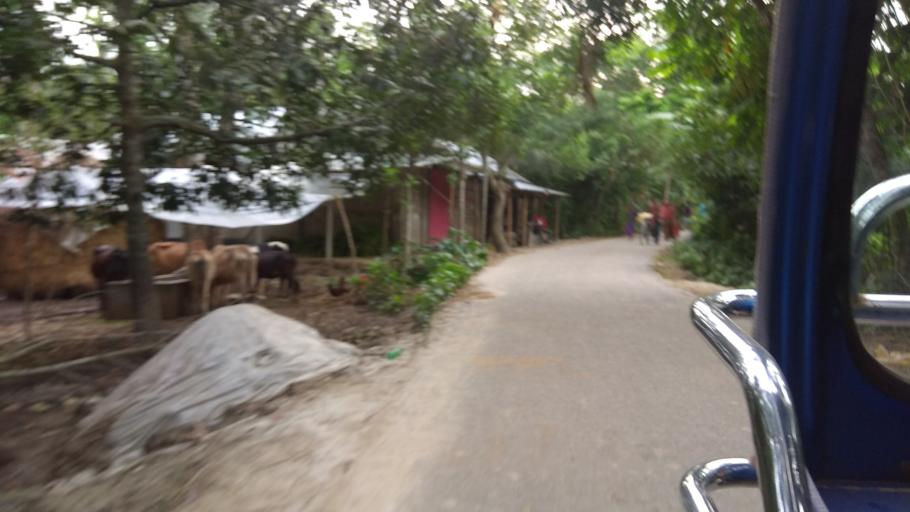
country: BD
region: Khulna
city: Kalia
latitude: 23.0383
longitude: 89.6626
